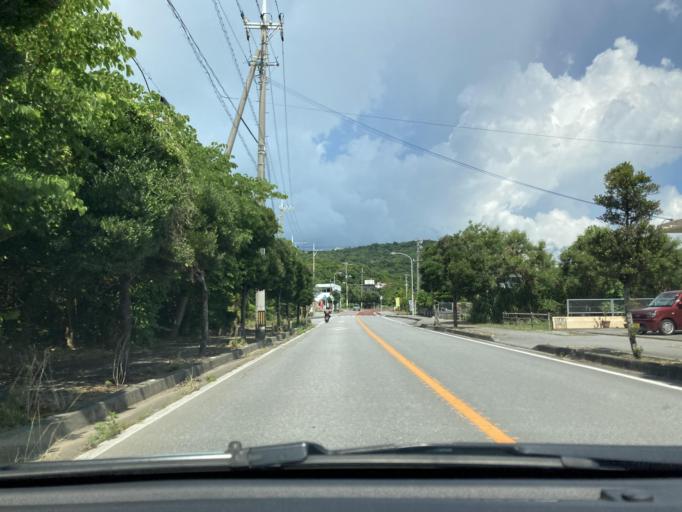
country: JP
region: Okinawa
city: Tomigusuku
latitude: 26.1746
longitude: 127.7680
